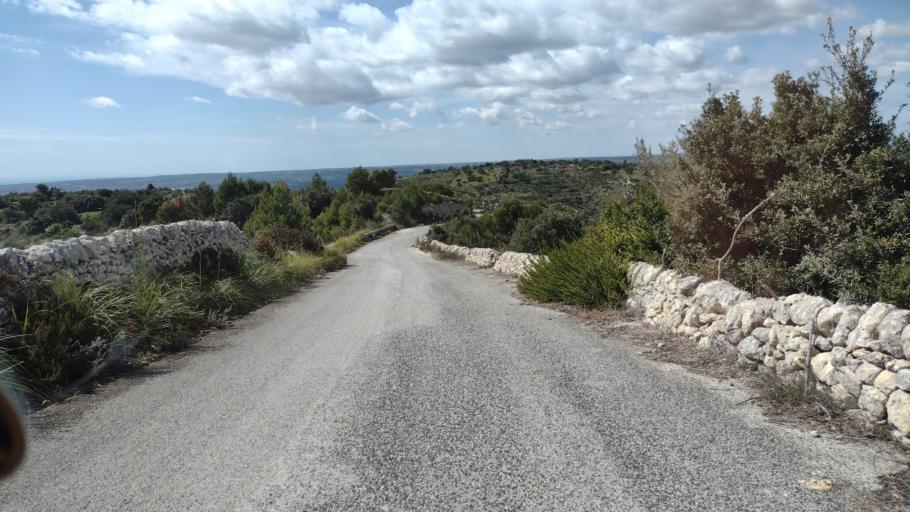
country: IT
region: Sicily
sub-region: Provincia di Siracusa
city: Rosolini
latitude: 36.9101
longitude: 14.9777
